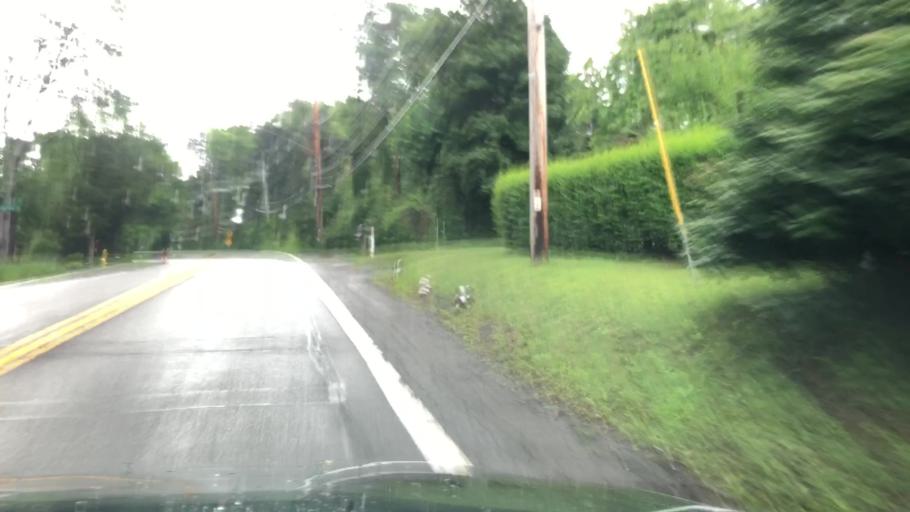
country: US
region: New York
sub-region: Dutchess County
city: Beacon
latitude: 41.5224
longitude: -73.9360
